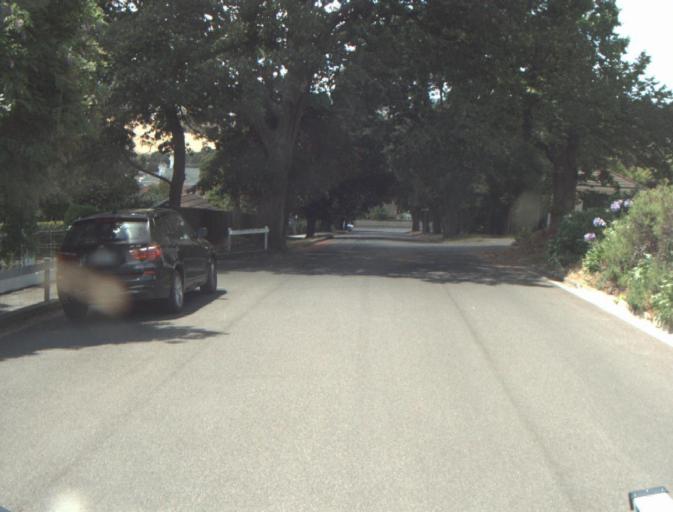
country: AU
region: Tasmania
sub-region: Launceston
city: East Launceston
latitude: -41.4383
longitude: 147.1561
